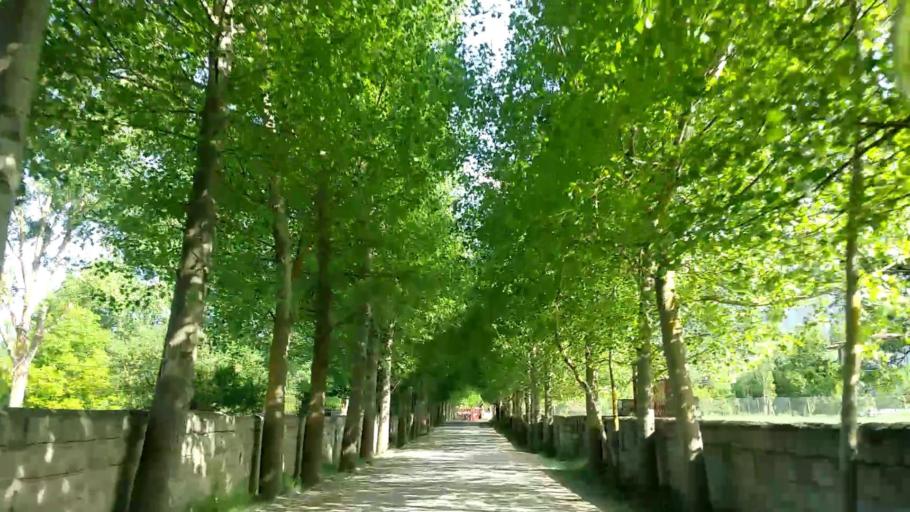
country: IR
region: Mazandaran
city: `Abbasabad
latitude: 36.5203
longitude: 51.1737
